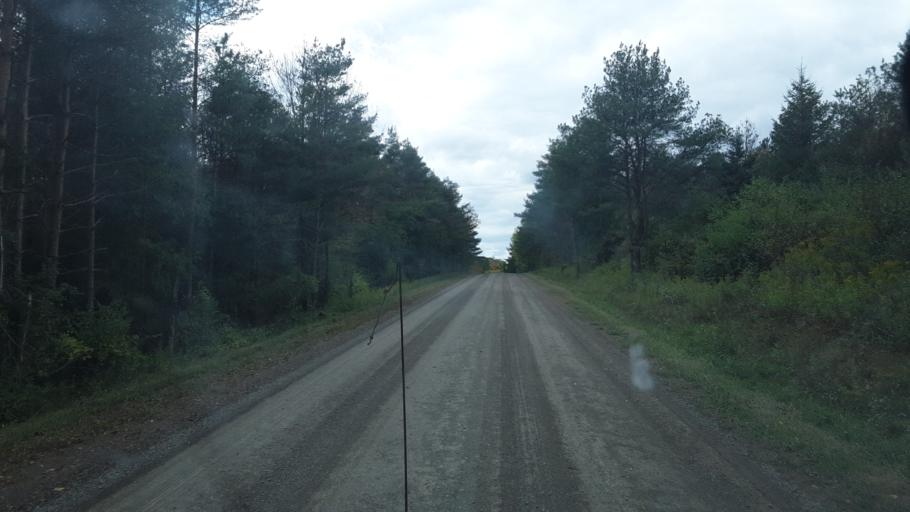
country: US
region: New York
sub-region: Allegany County
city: Alfred
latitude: 42.3909
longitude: -77.8744
